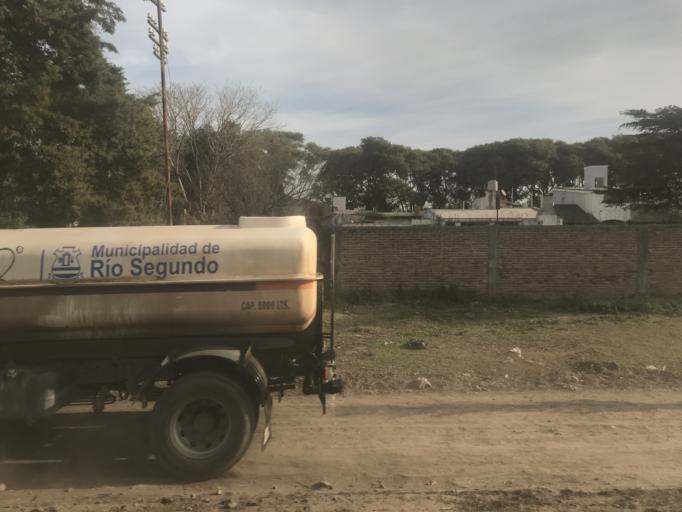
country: AR
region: Cordoba
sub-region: Departamento de Rio Segundo
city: Rio Segundo
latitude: -31.6496
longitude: -63.9140
